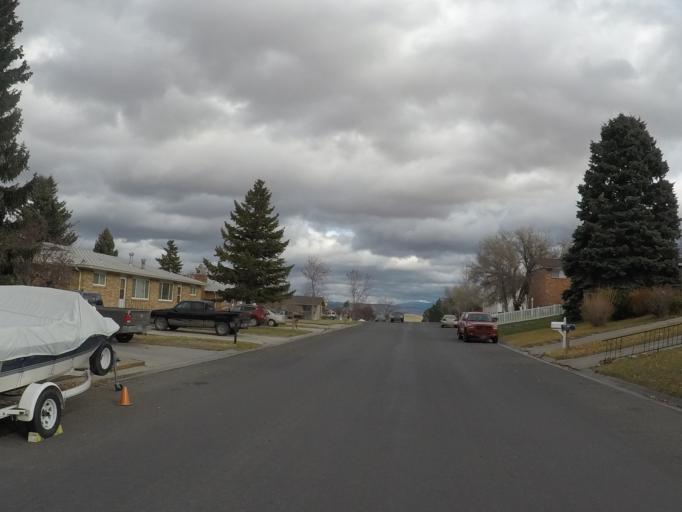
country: US
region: Montana
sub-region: Lewis and Clark County
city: Helena
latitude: 46.5814
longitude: -112.0064
